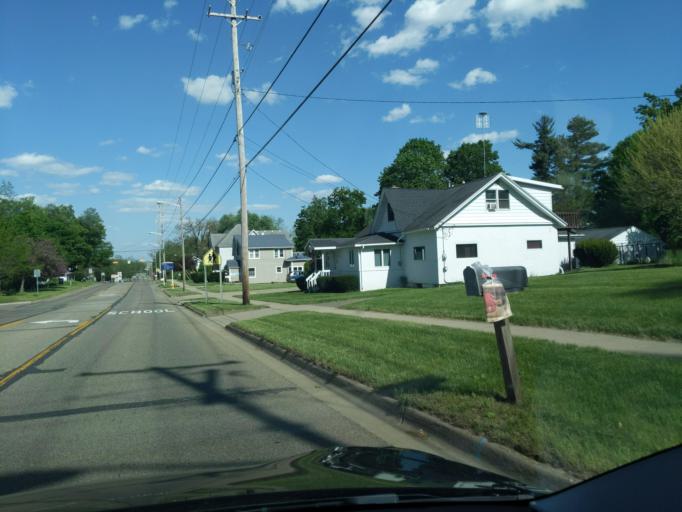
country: US
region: Michigan
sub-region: Ionia County
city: Lake Odessa
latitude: 42.7775
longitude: -85.1401
